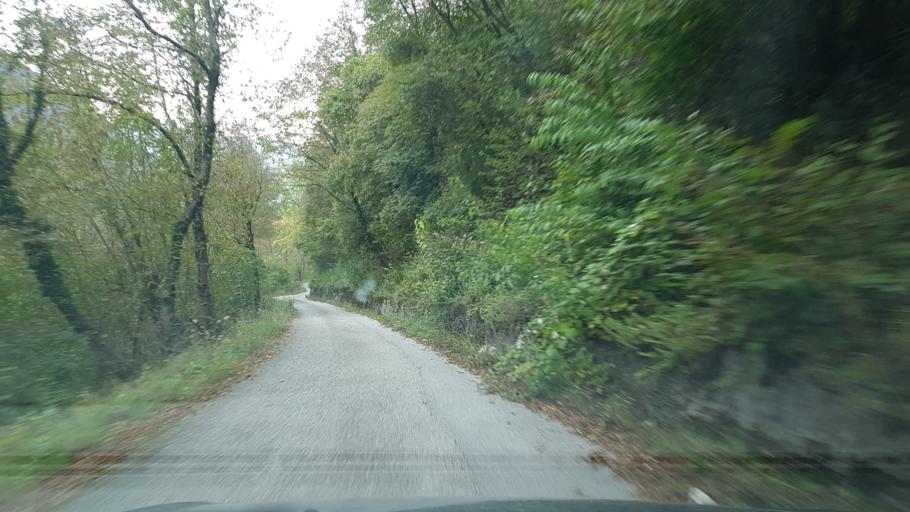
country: IT
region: Friuli Venezia Giulia
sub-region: Provincia di Udine
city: Venzone
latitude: 46.3346
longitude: 13.1578
